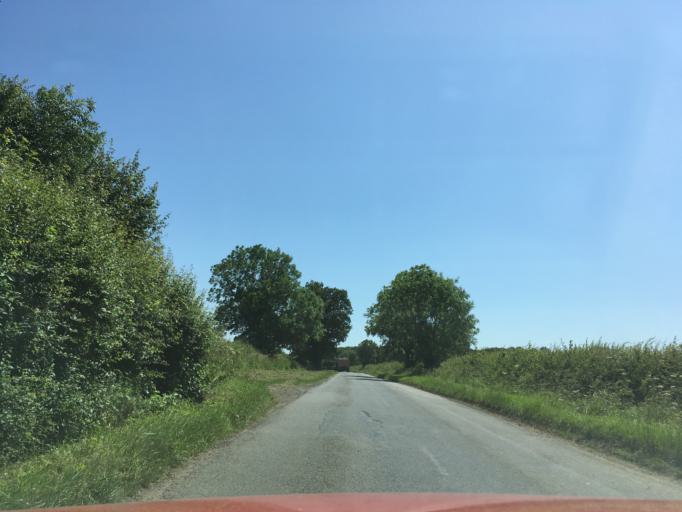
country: GB
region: England
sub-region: Northamptonshire
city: Deanshanger
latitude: 52.0082
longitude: -0.8937
